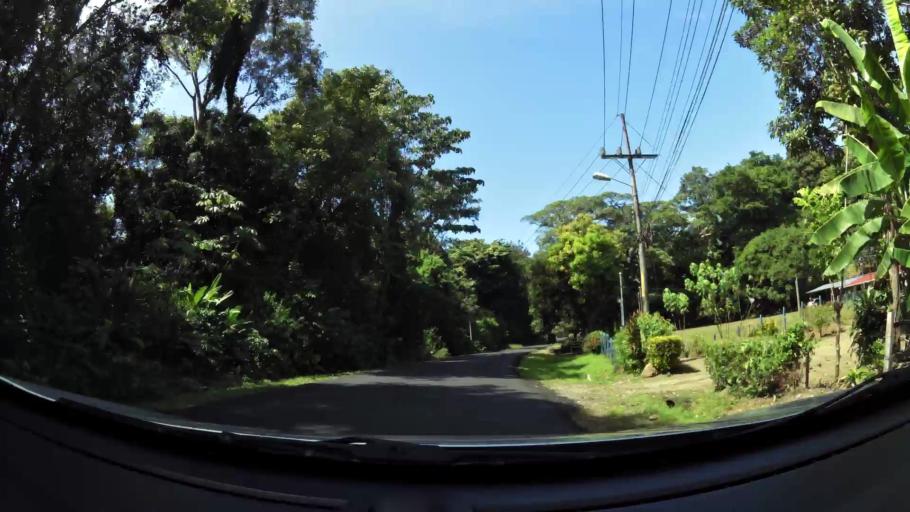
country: CR
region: San Jose
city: San Isidro
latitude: 9.2807
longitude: -83.8437
